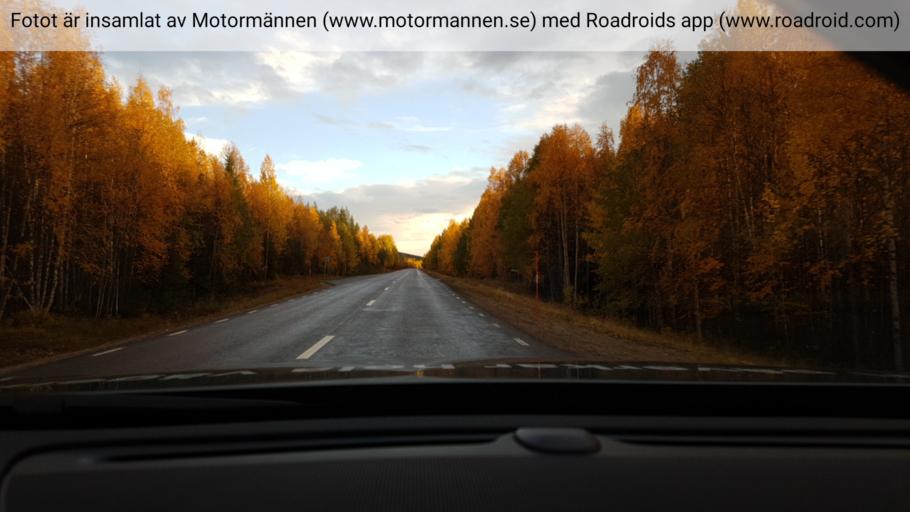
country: SE
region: Norrbotten
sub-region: Overkalix Kommun
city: OEverkalix
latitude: 66.5868
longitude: 22.7566
